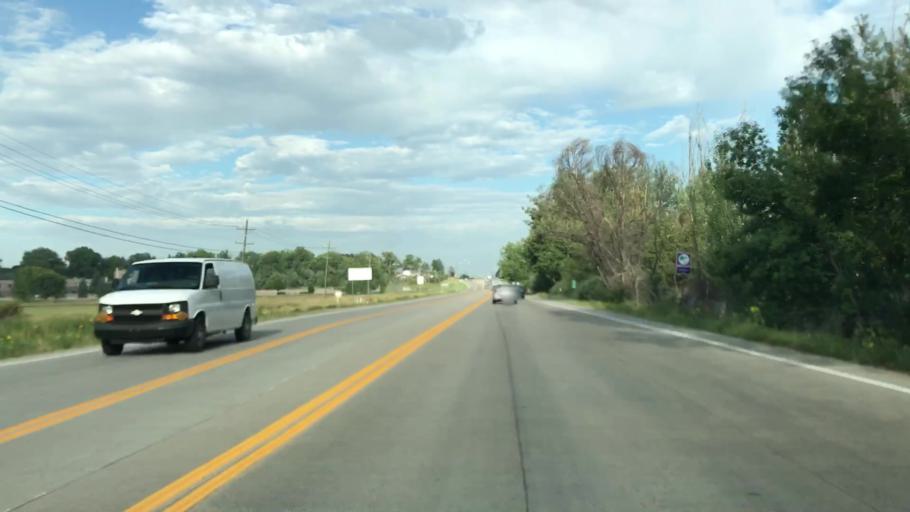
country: US
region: Colorado
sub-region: Boulder County
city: Longmont
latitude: 40.2031
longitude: -105.1150
